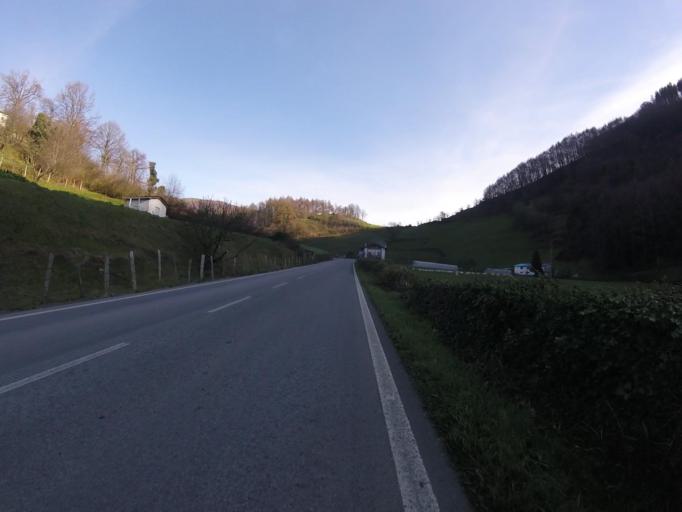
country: ES
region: Navarre
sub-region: Provincia de Navarra
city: Leitza
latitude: 43.0837
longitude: -1.9107
